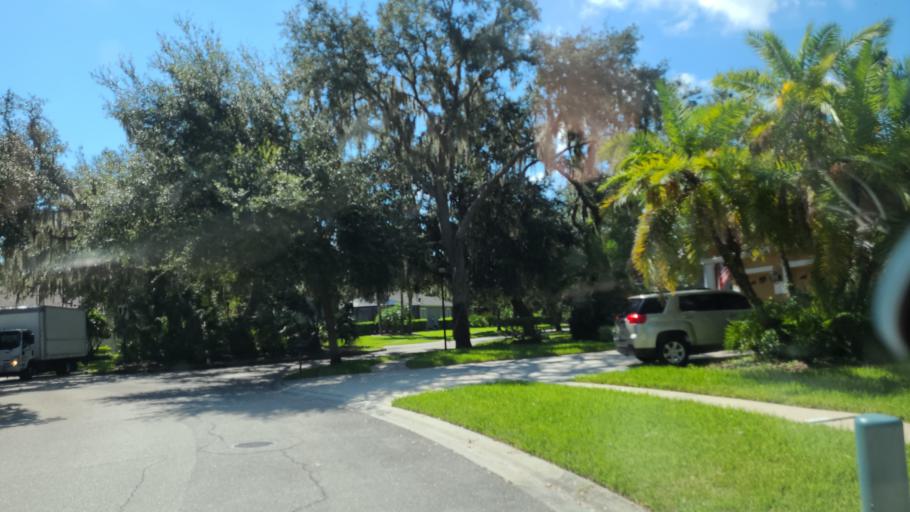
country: US
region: Florida
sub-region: Hillsborough County
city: Fish Hawk
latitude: 27.8394
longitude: -82.2242
